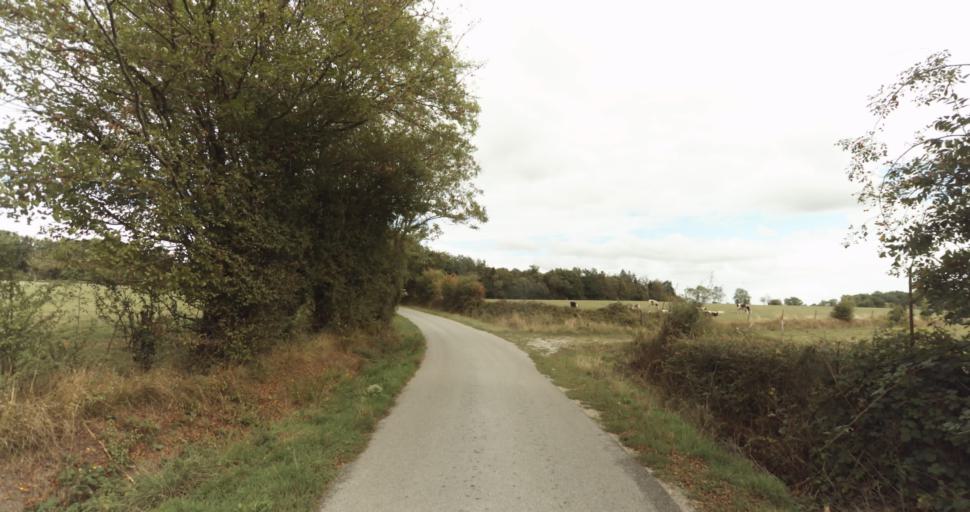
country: FR
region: Lower Normandy
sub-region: Departement de l'Orne
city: Sainte-Gauburge-Sainte-Colombe
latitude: 48.7751
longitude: 0.3832
